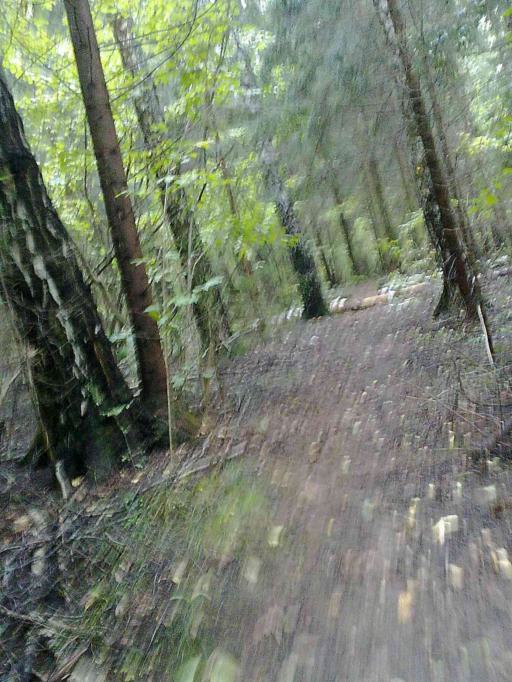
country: RU
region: Moskovskaya
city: Gorki Vtoryye
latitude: 55.6844
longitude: 37.1544
